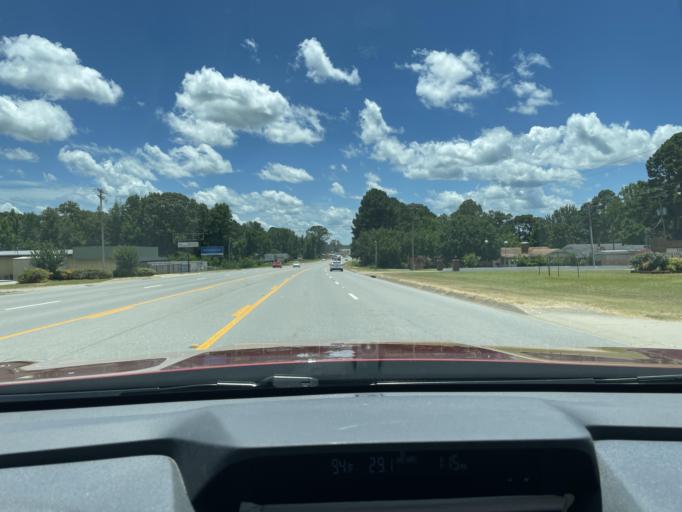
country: US
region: Arkansas
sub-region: Drew County
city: Monticello
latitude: 33.6457
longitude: -91.8011
